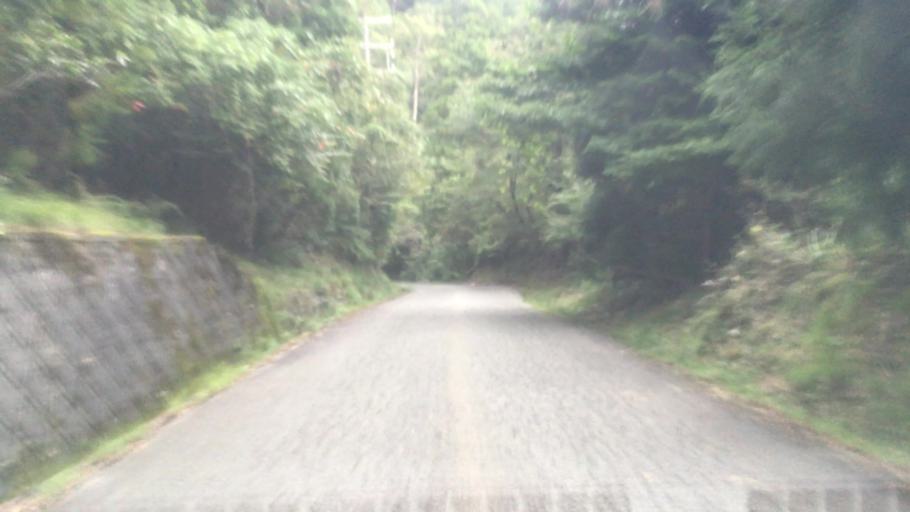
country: JP
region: Hyogo
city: Toyooka
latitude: 35.6208
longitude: 134.8767
